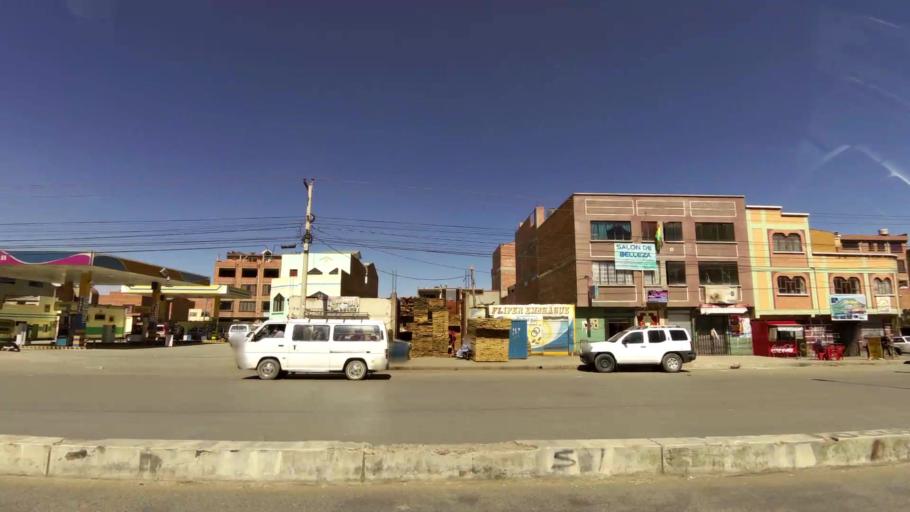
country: BO
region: La Paz
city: La Paz
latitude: -16.4924
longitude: -68.1984
